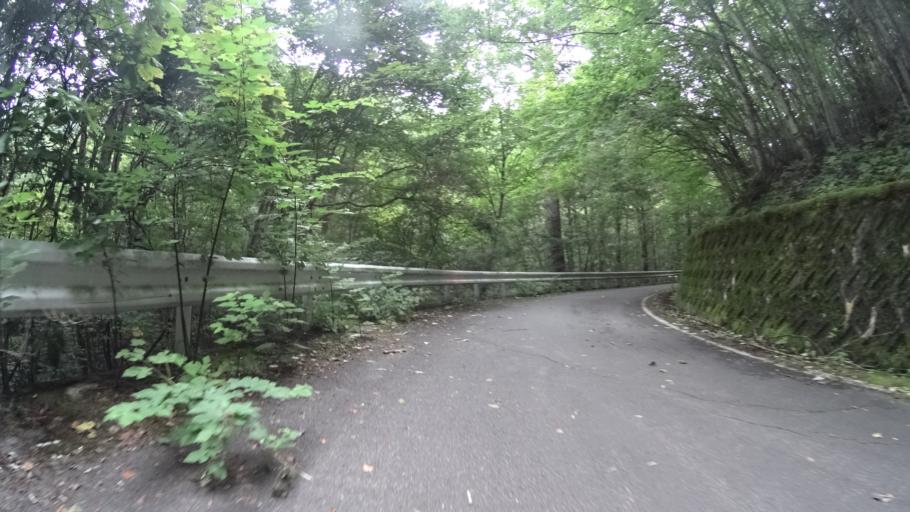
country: JP
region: Yamanashi
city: Kofu-shi
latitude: 35.8056
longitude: 138.6178
